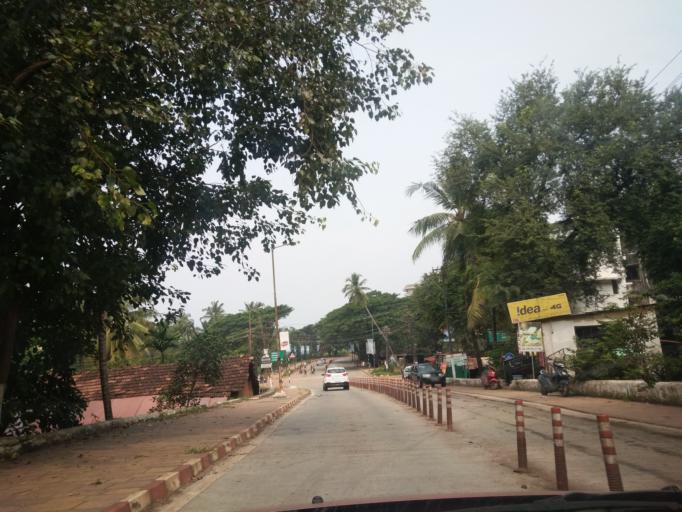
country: IN
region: Goa
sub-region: North Goa
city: Taleigao
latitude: 15.4589
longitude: 73.8035
